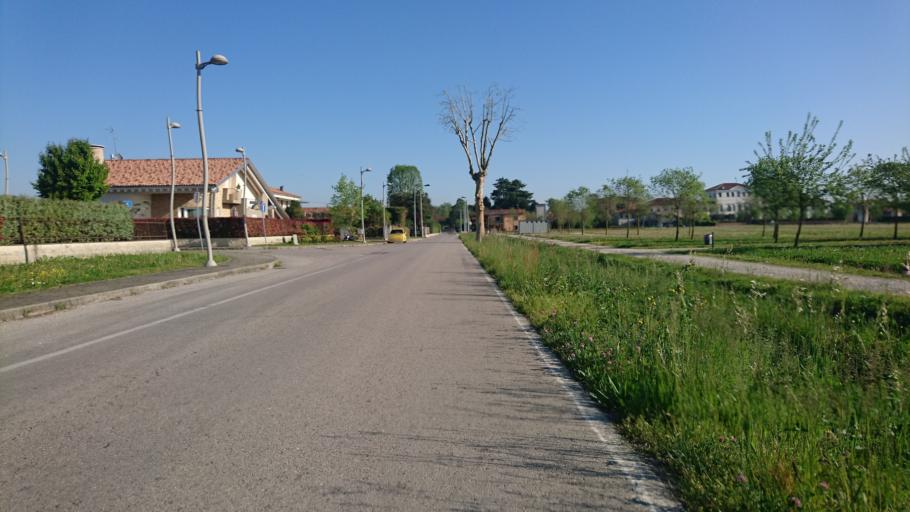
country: IT
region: Veneto
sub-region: Provincia di Padova
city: Massanzago-Ca' Baglioni-San Dono
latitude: 45.5531
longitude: 12.0029
